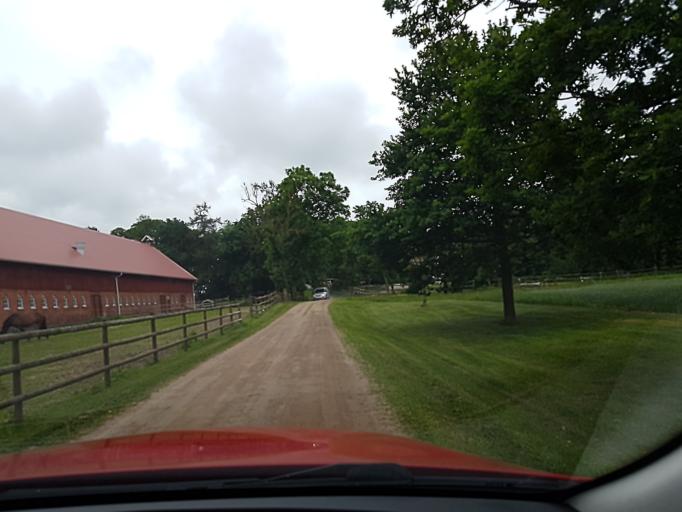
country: SE
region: Vaestra Goetaland
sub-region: Tibro Kommun
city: Tibro
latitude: 58.2980
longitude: 14.1359
